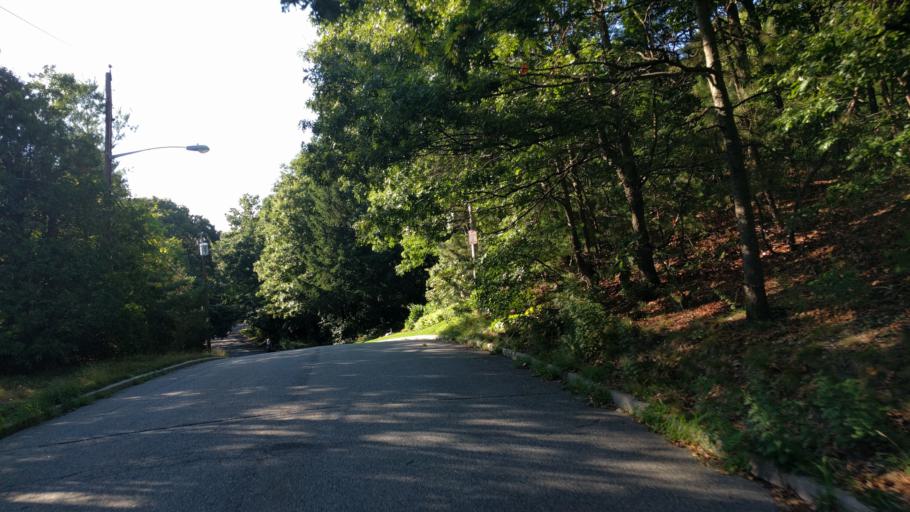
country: US
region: New York
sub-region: Nassau County
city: East Norwich
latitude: 40.8491
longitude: -73.5308
